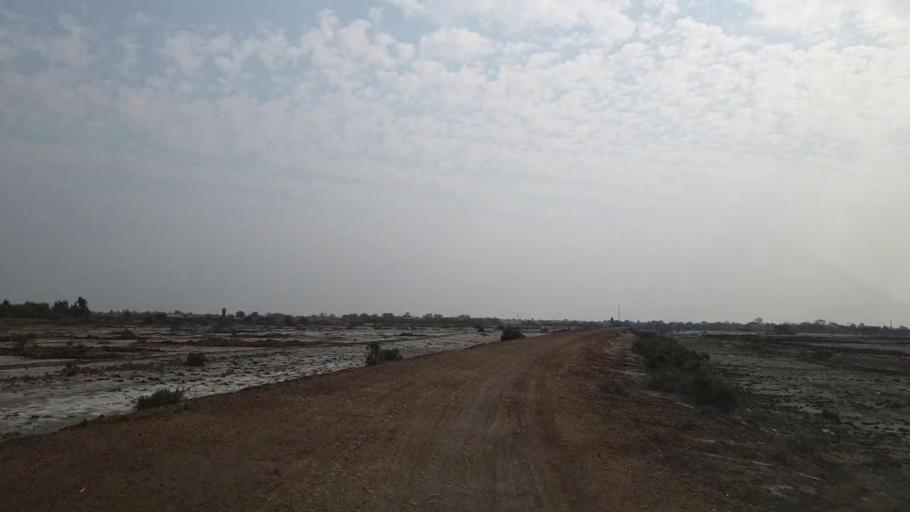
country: PK
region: Sindh
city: Mirpur Khas
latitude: 25.5544
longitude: 69.1596
